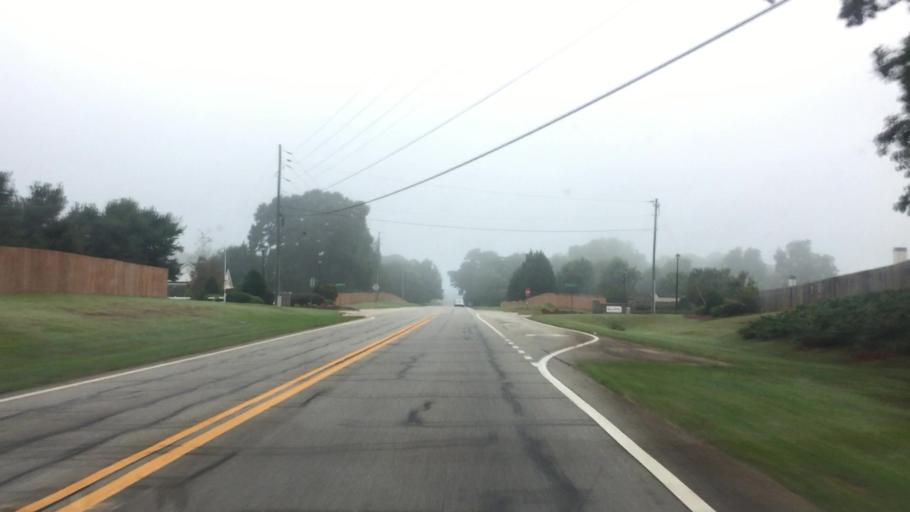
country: US
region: Georgia
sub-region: Henry County
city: Stockbridge
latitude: 33.5772
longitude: -84.1475
